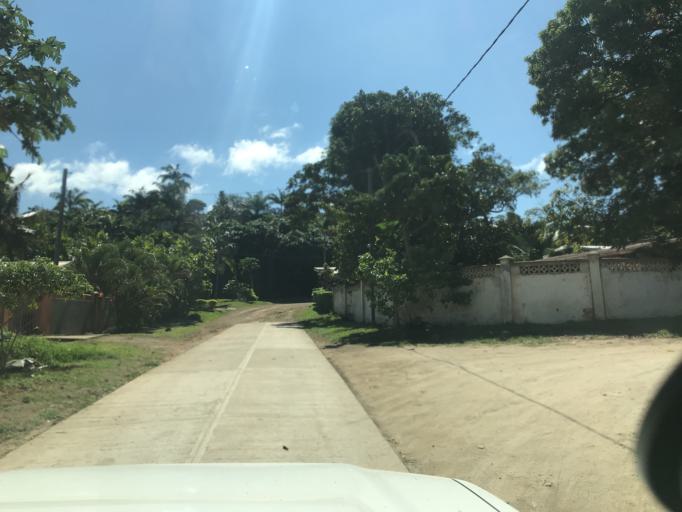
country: VU
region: Sanma
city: Luganville
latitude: -15.5132
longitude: 167.1833
